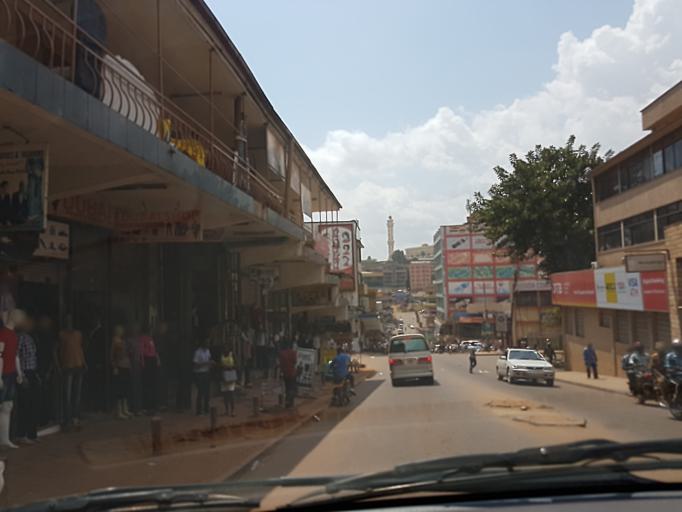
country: UG
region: Central Region
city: Kampala Central Division
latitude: 0.3178
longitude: 32.5738
